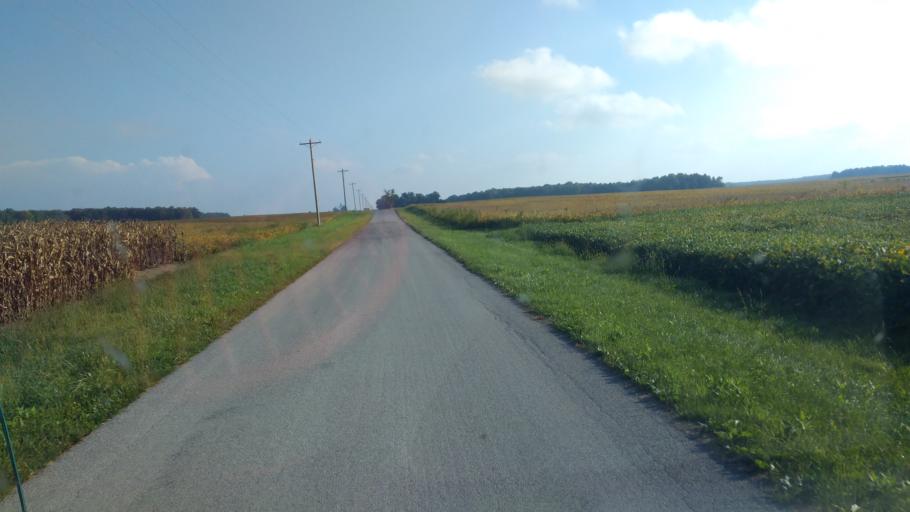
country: US
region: Ohio
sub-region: Wyandot County
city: Upper Sandusky
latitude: 40.7601
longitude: -83.3241
